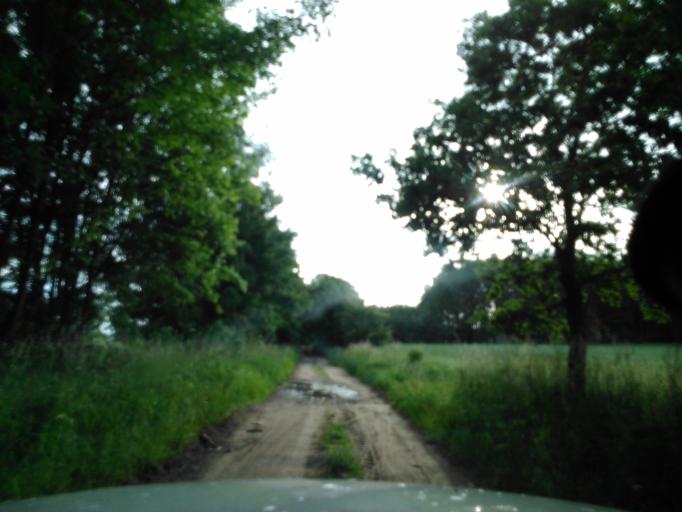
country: PL
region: Pomeranian Voivodeship
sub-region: Powiat slupski
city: Smoldzino
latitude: 54.6307
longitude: 17.2777
